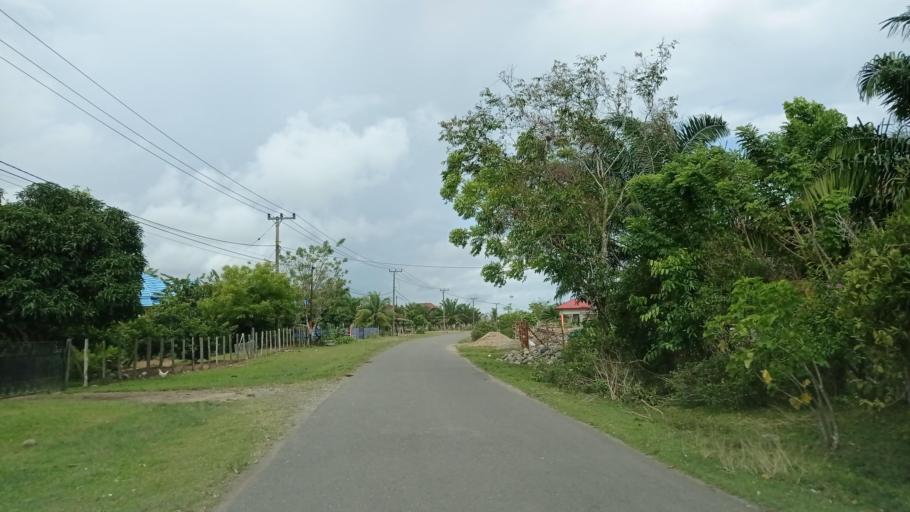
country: ID
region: Bengkulu
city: Ipuh
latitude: -2.5694
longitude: 101.1175
